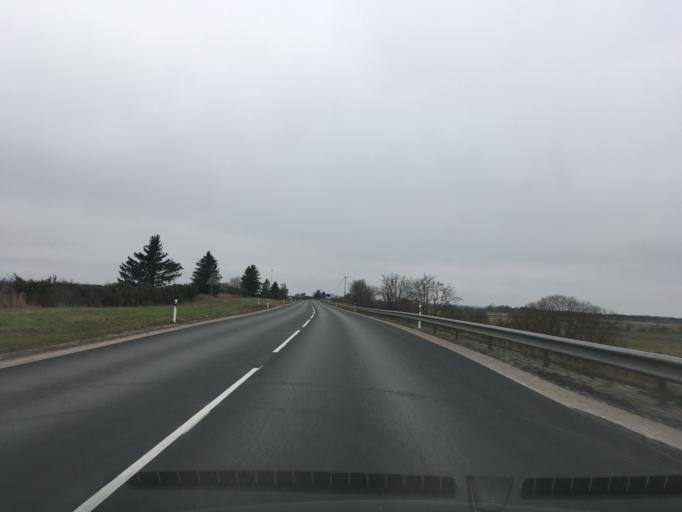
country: EE
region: Ida-Virumaa
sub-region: Aseri vald
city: Aseri
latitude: 59.4425
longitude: 26.7942
